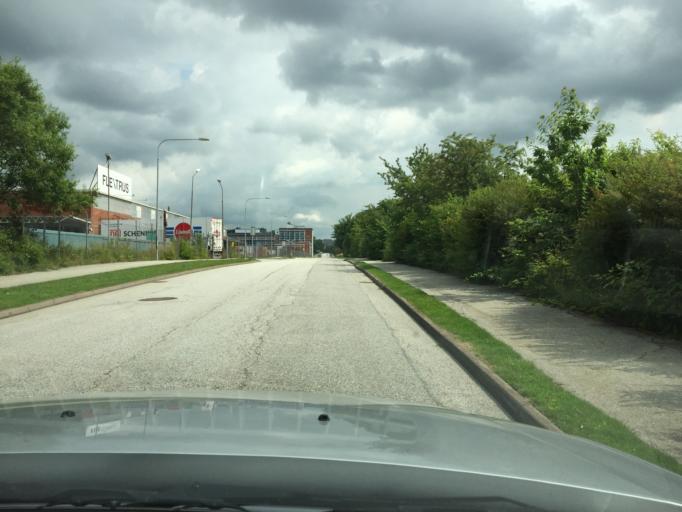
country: SE
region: Skane
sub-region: Lunds Kommun
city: Lund
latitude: 55.6935
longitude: 13.1688
